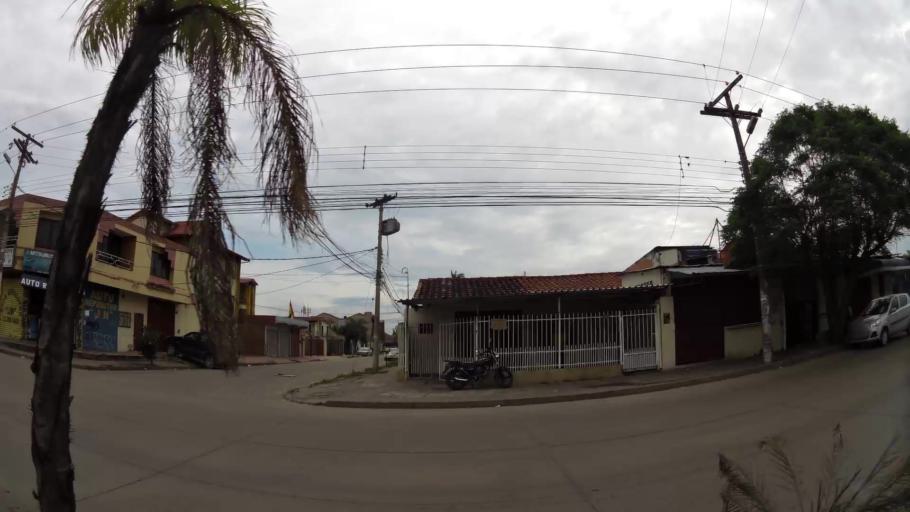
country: BO
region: Santa Cruz
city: Santa Cruz de la Sierra
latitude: -17.7610
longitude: -63.1581
